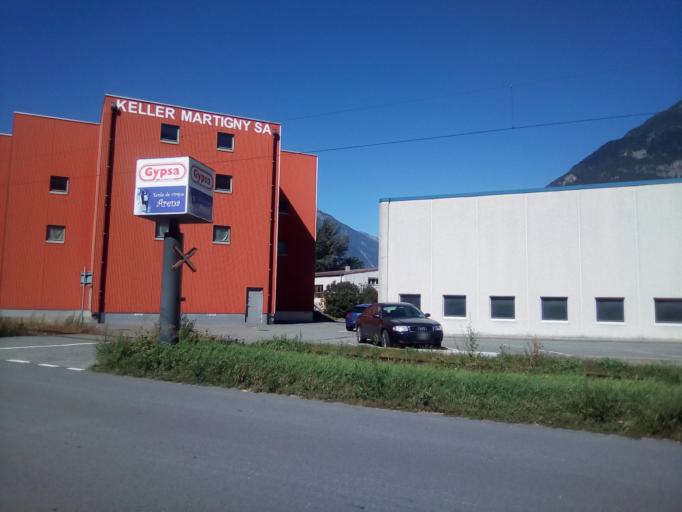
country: CH
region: Valais
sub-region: Martigny District
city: Martigny-Ville
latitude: 46.1067
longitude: 7.0919
